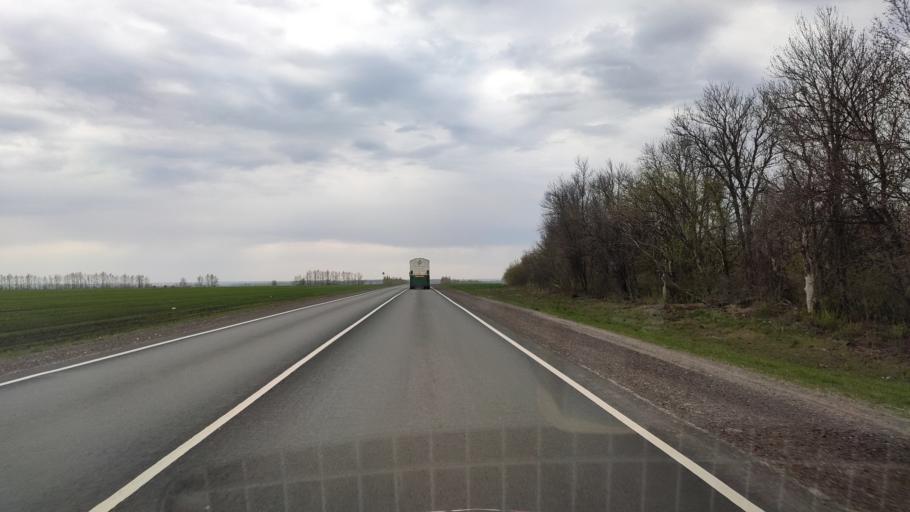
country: RU
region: Voronezj
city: Nizhnedevitsk
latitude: 51.6099
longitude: 38.6122
